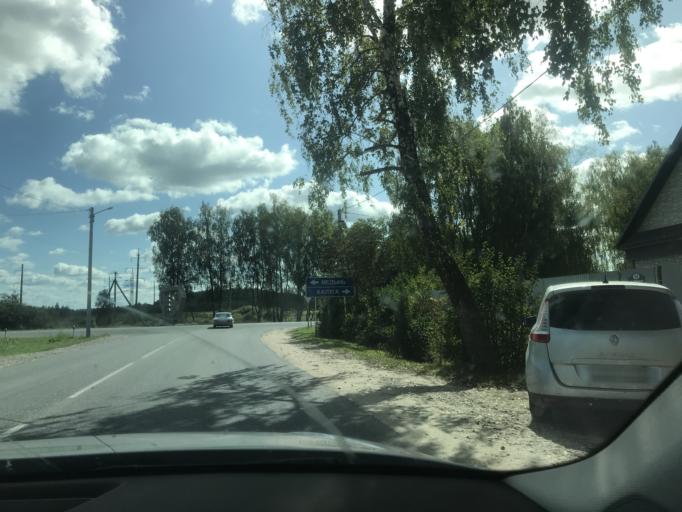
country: RU
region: Kaluga
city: Kondrovo
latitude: 54.8026
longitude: 35.9516
